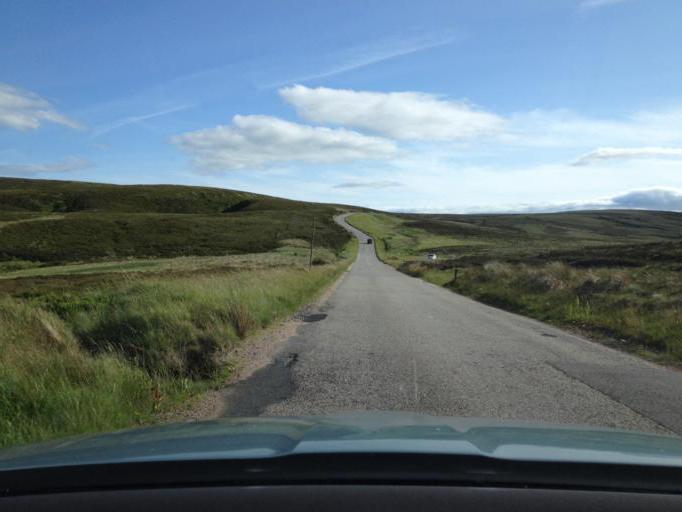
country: GB
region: Scotland
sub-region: Aberdeenshire
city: Laurencekirk
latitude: 56.9268
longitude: -2.5788
